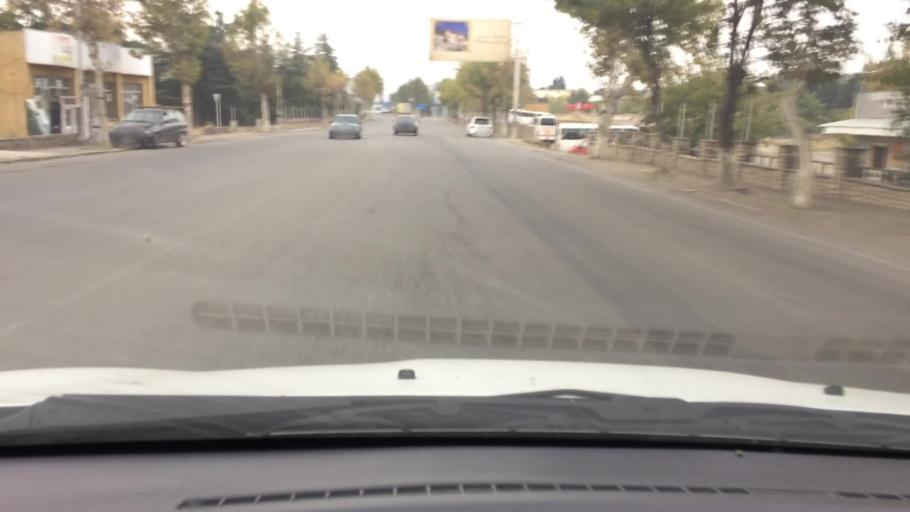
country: GE
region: Kvemo Kartli
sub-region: Marneuli
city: Marneuli
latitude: 41.4910
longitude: 44.8016
